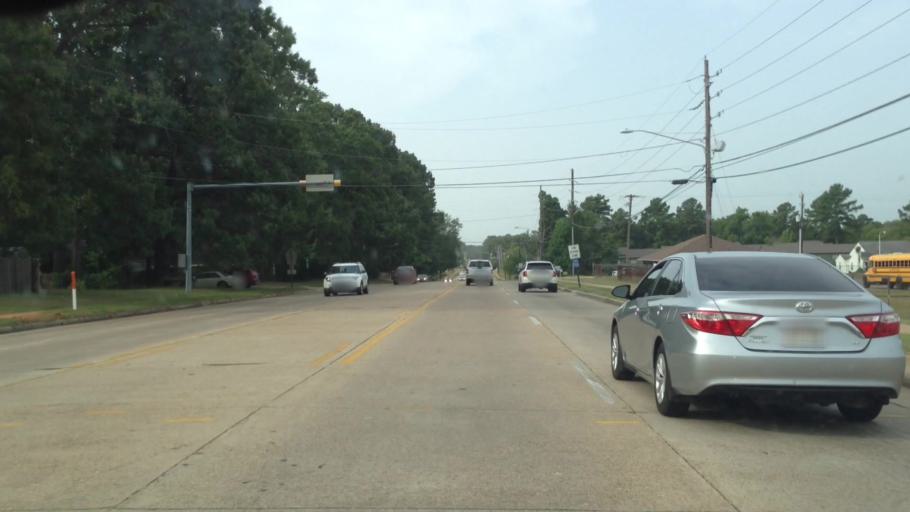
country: US
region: Louisiana
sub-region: De Soto Parish
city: Stonewall
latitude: 32.4073
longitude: -93.8147
